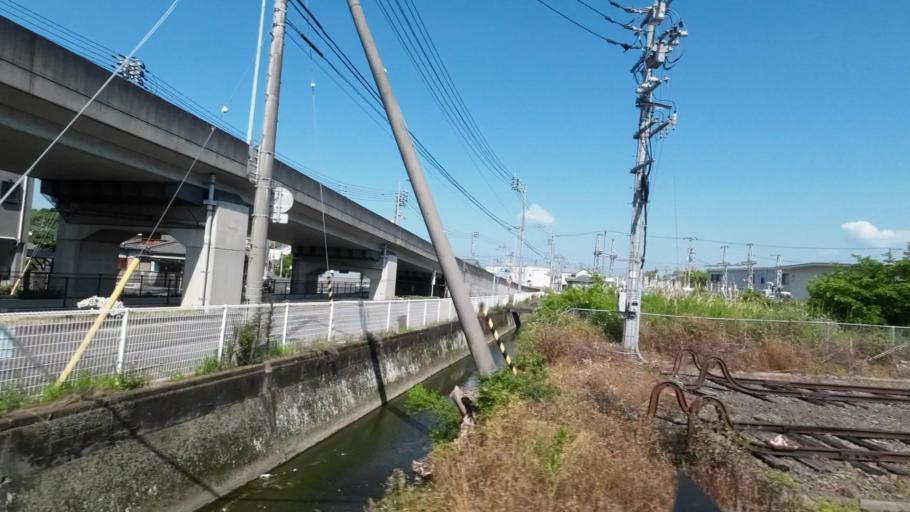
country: JP
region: Kagawa
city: Tadotsu
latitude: 34.2678
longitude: 133.7552
